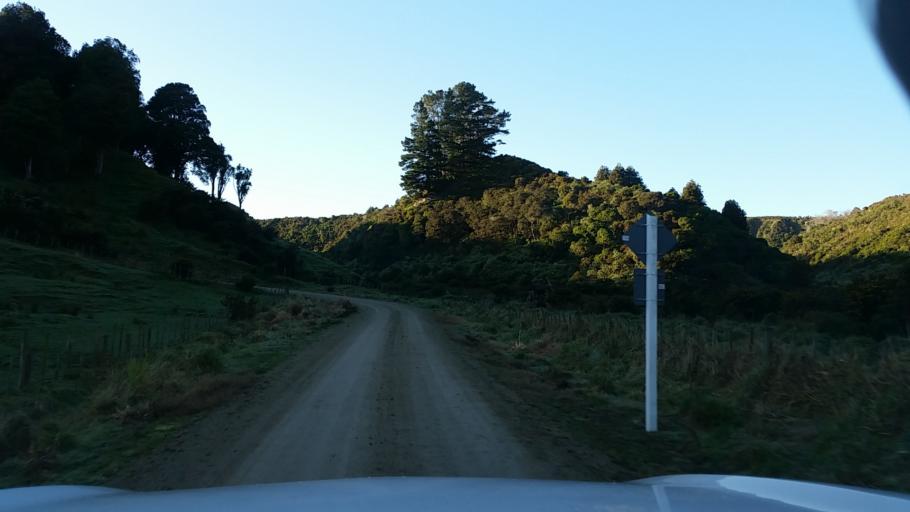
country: NZ
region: Taranaki
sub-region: South Taranaki District
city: Patea
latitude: -39.7605
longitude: 174.7348
